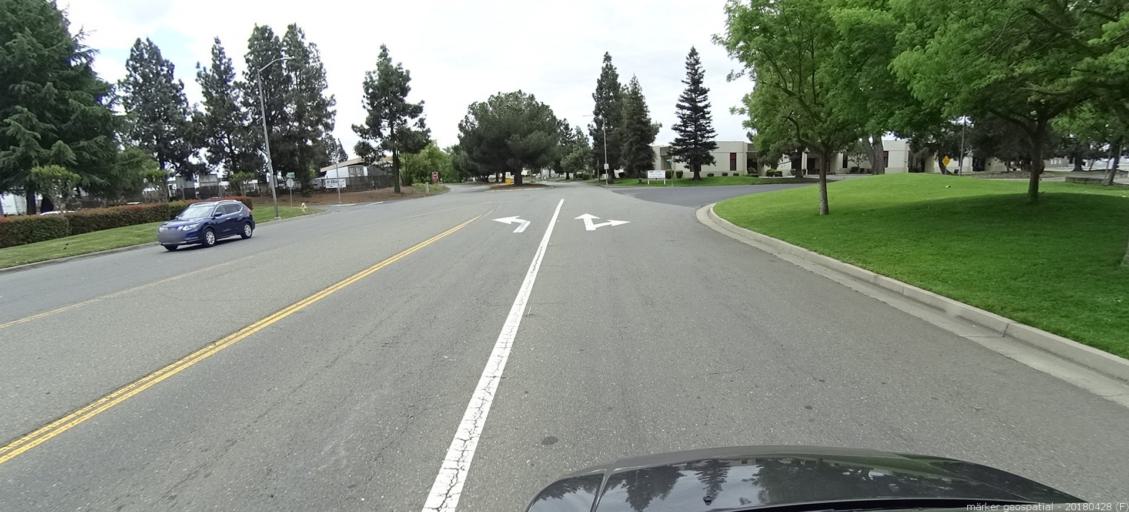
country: US
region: California
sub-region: Yolo County
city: West Sacramento
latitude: 38.5648
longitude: -121.5786
